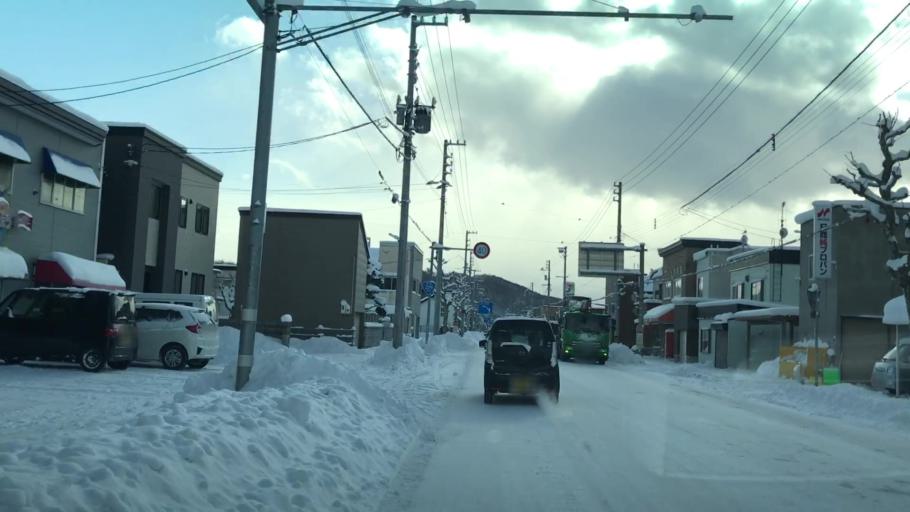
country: JP
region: Hokkaido
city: Yoichi
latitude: 43.2077
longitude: 140.7713
